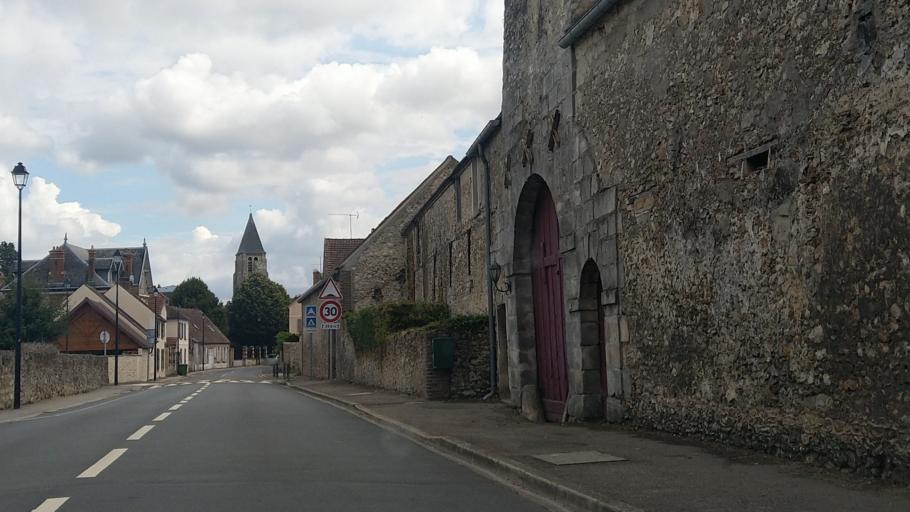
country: FR
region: Ile-de-France
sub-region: Departement des Yvelines
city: Sonchamp
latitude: 48.5783
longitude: 1.8745
